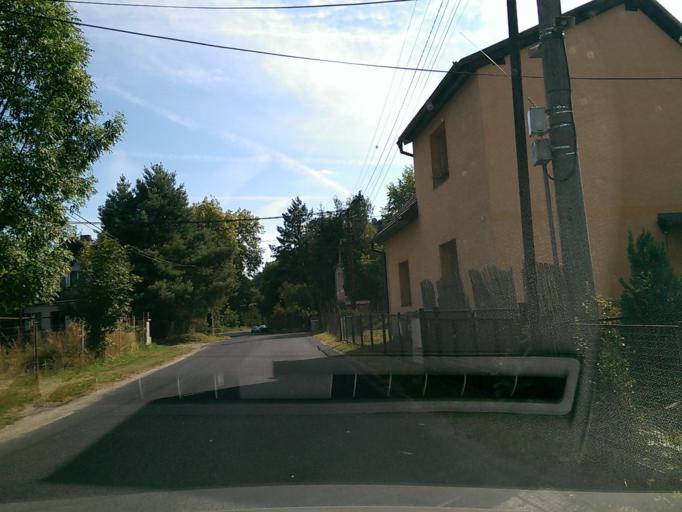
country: CZ
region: Central Bohemia
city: Bakov nad Jizerou
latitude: 50.4687
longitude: 14.9187
